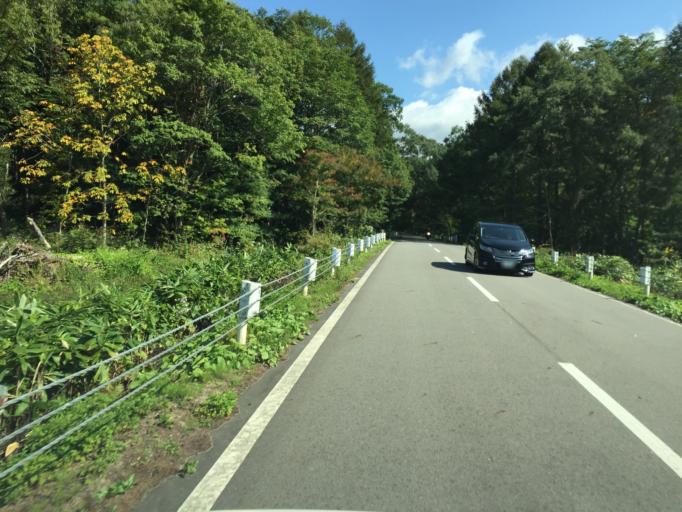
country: JP
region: Fukushima
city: Inawashiro
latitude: 37.6520
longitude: 140.1986
